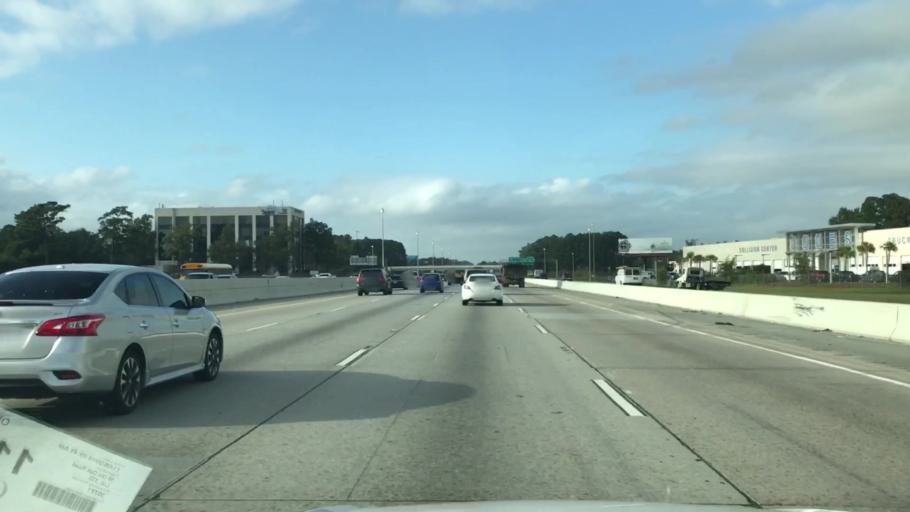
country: US
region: South Carolina
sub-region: Berkeley County
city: Hanahan
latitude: 32.8987
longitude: -80.0206
